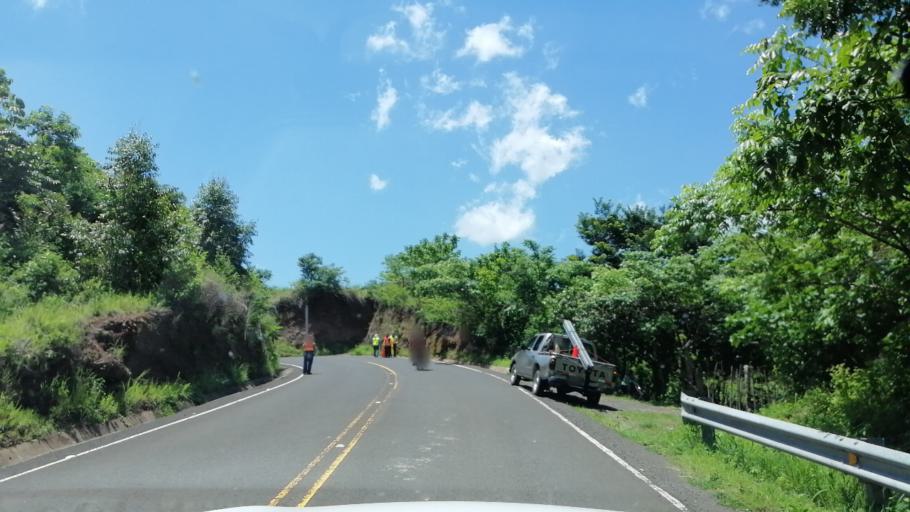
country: SV
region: San Miguel
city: Ciudad Barrios
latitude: 13.7906
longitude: -88.2888
